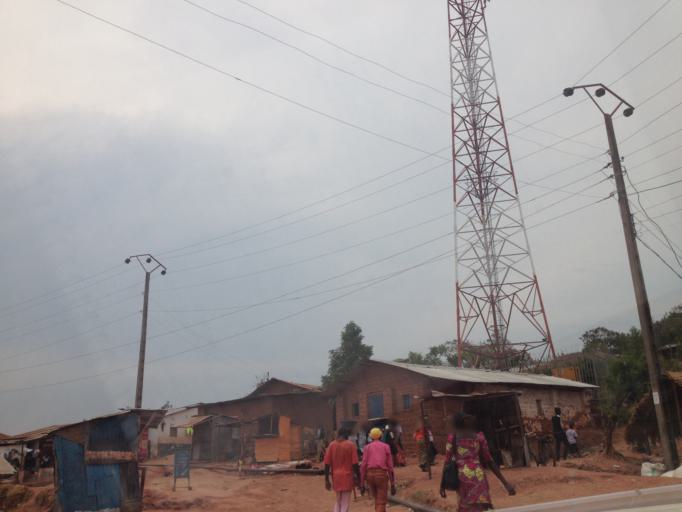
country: CD
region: Katanga
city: Kalemie
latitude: -5.9352
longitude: 29.1797
